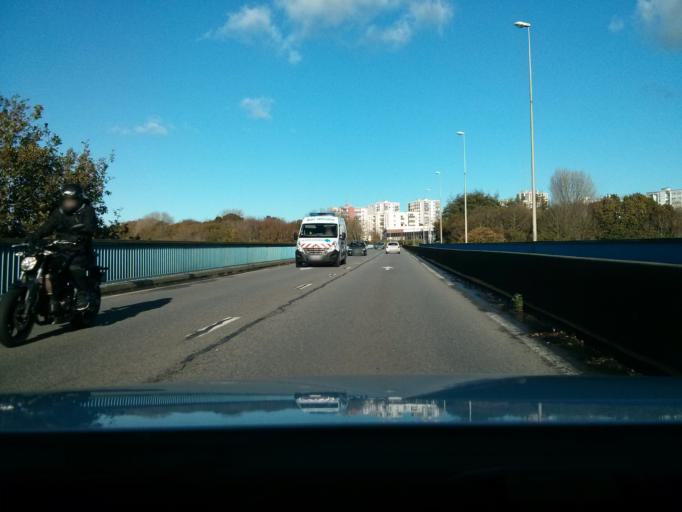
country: FR
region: Brittany
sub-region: Departement du Finistere
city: Bohars
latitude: 48.4038
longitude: -4.5237
